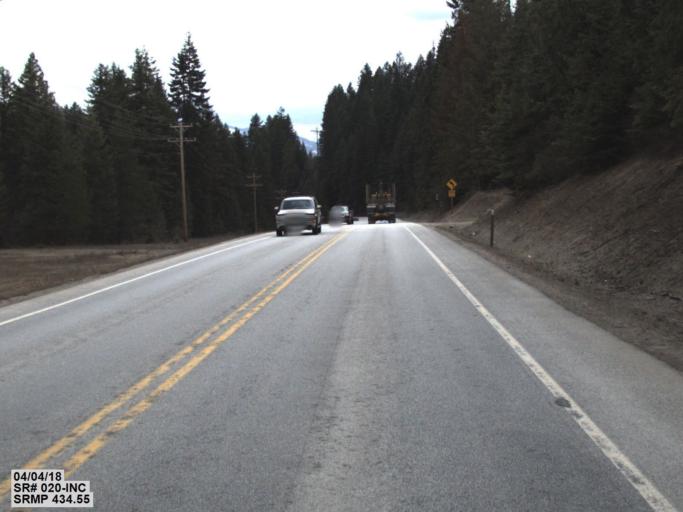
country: US
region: Washington
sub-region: Pend Oreille County
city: Newport
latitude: 48.2118
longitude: -117.0687
